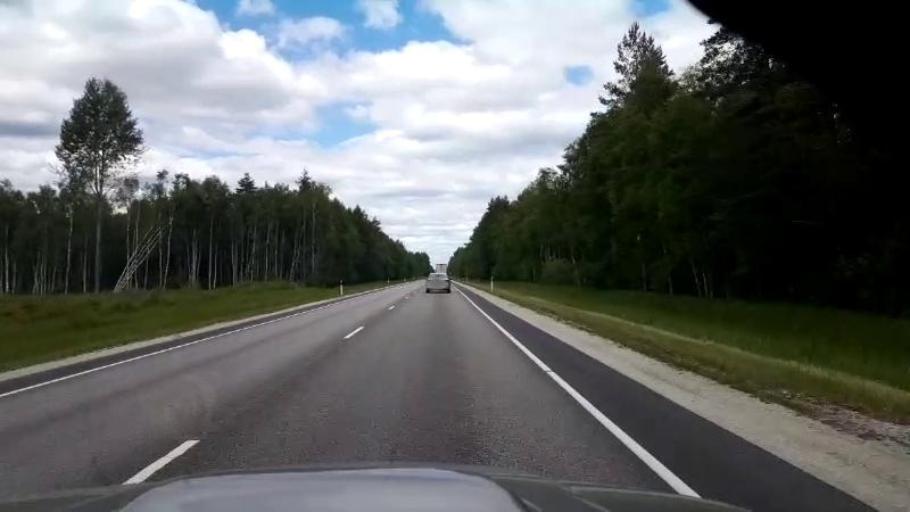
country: EE
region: Paernumaa
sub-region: Halinga vald
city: Parnu-Jaagupi
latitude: 58.7230
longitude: 24.4237
